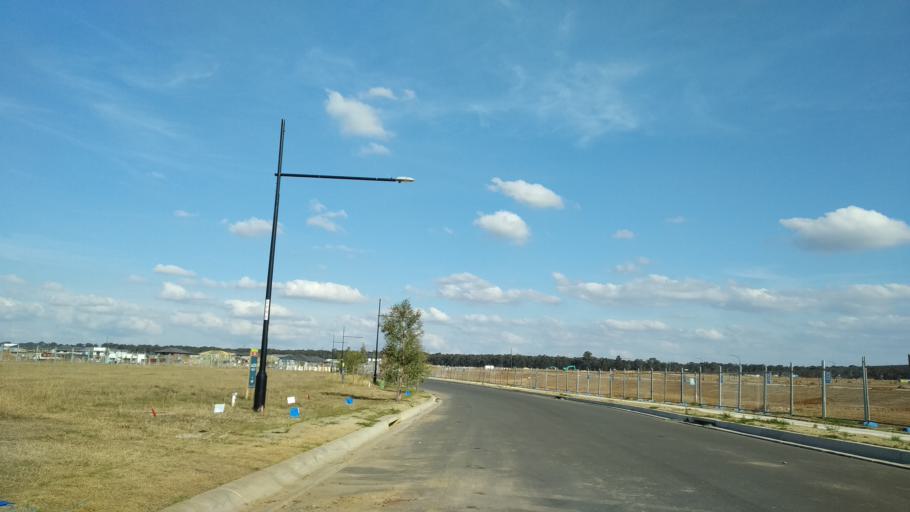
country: AU
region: New South Wales
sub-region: Blacktown
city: Blackett
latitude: -33.6964
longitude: 150.8067
